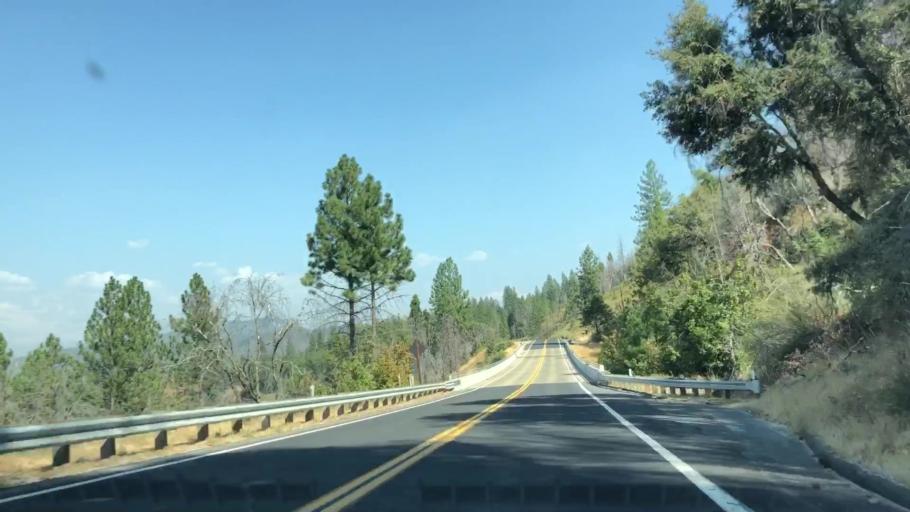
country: US
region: California
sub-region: Tuolumne County
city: Tuolumne City
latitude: 37.8218
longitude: -120.0372
